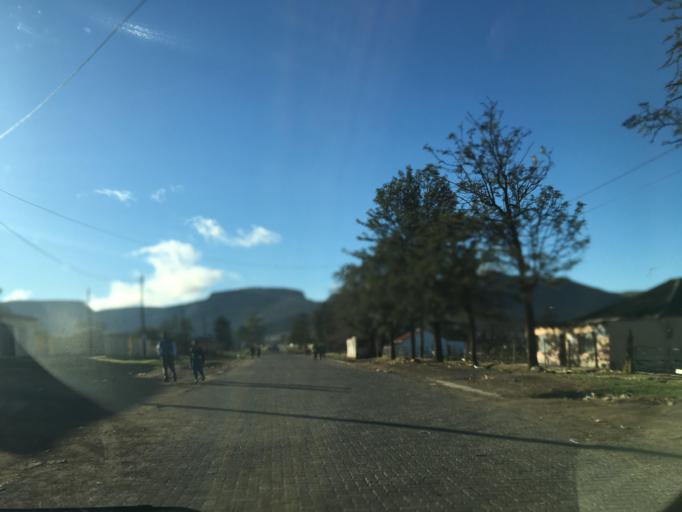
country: ZA
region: Eastern Cape
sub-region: Chris Hani District Municipality
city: Cala
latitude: -31.5261
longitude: 27.6951
